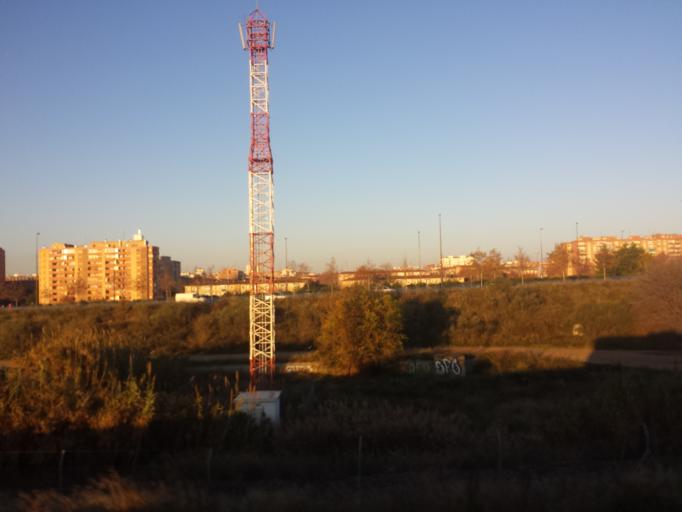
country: ES
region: Aragon
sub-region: Provincia de Zaragoza
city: Zaragoza
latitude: 41.6460
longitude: -0.8582
